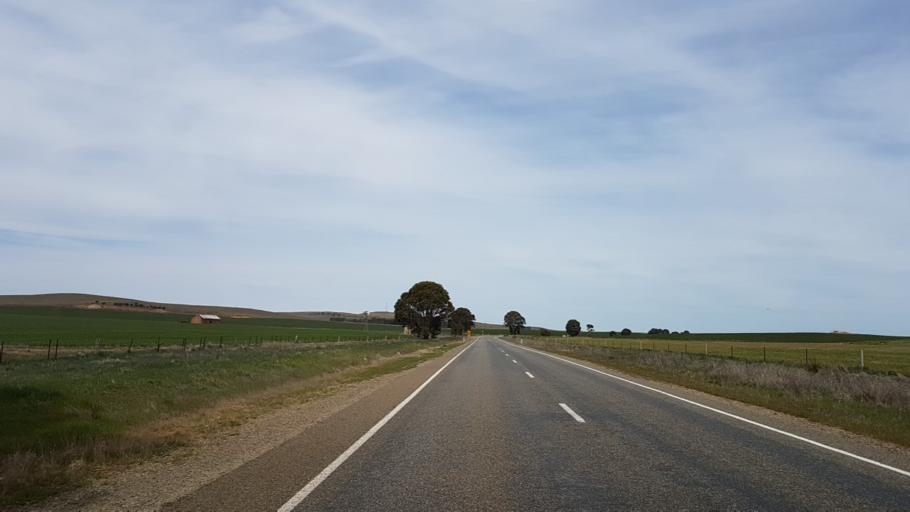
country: AU
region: South Australia
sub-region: Northern Areas
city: Jamestown
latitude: -33.0859
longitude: 138.6187
